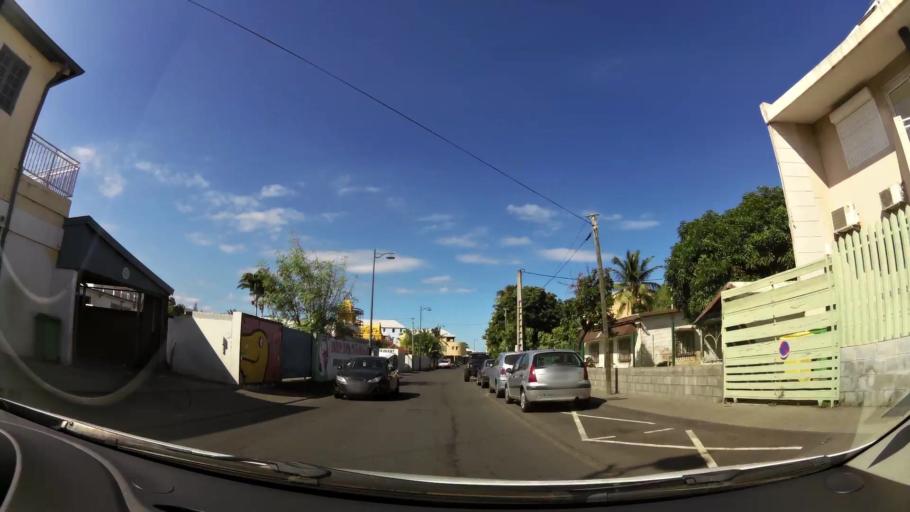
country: RE
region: Reunion
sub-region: Reunion
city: Saint-Pierre
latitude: -21.3371
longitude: 55.4593
